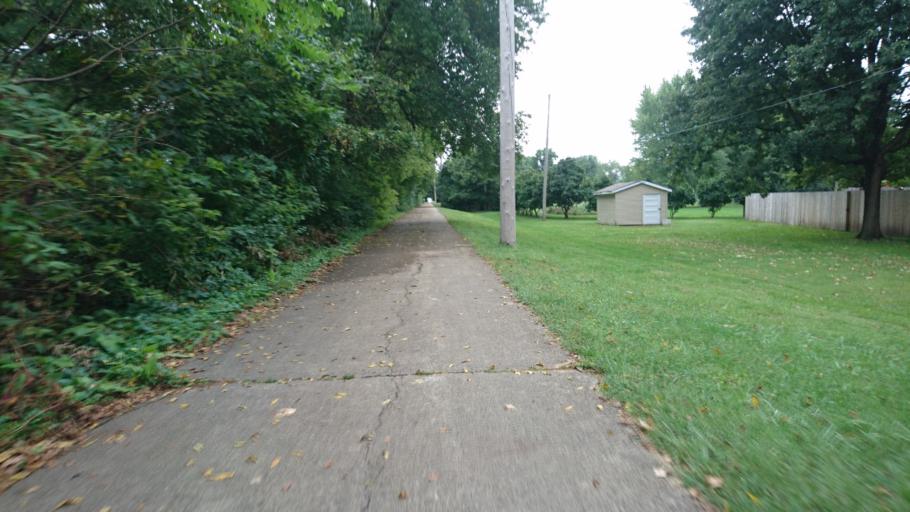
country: US
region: Illinois
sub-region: Sangamon County
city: Chatham
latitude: 39.6802
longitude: -89.7008
